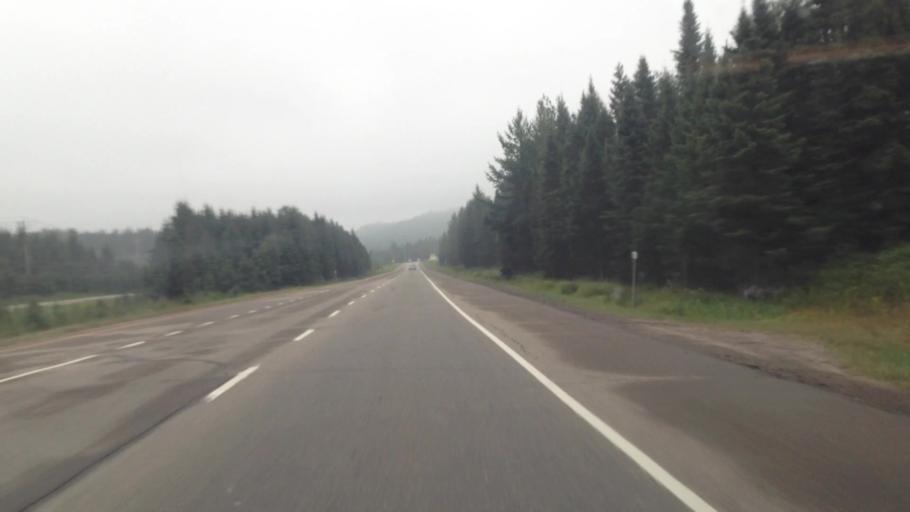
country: CA
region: Quebec
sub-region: Laurentides
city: Sainte-Agathe-des-Monts
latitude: 46.1019
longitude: -74.3813
